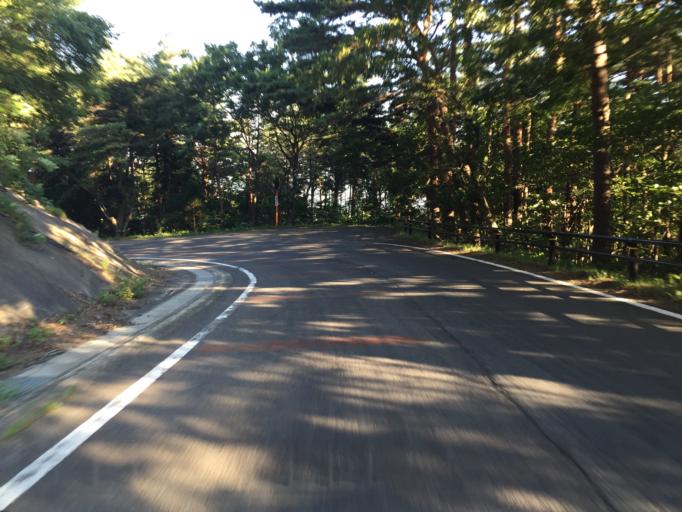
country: JP
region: Fukushima
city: Hobaramachi
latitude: 37.8979
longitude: 140.5154
